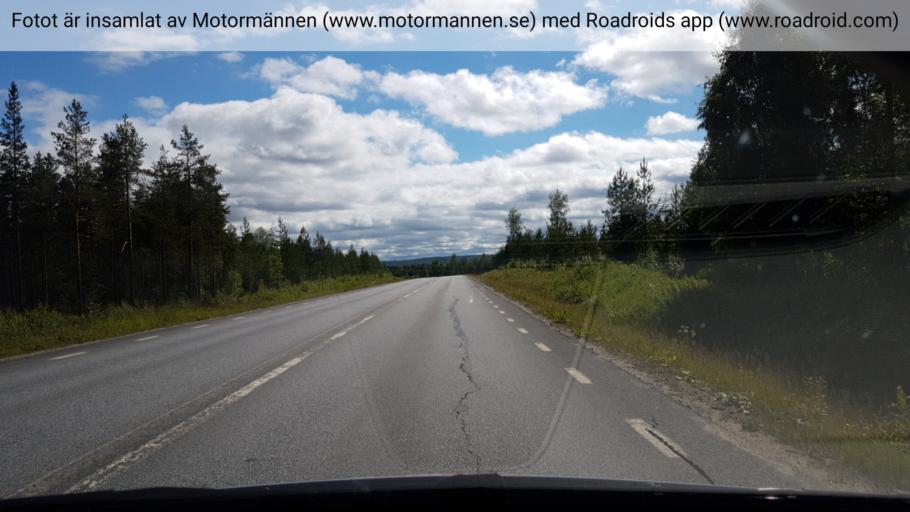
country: SE
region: Vaesterbotten
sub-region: Vannas Kommun
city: Vaennaes
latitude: 63.9879
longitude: 19.7316
